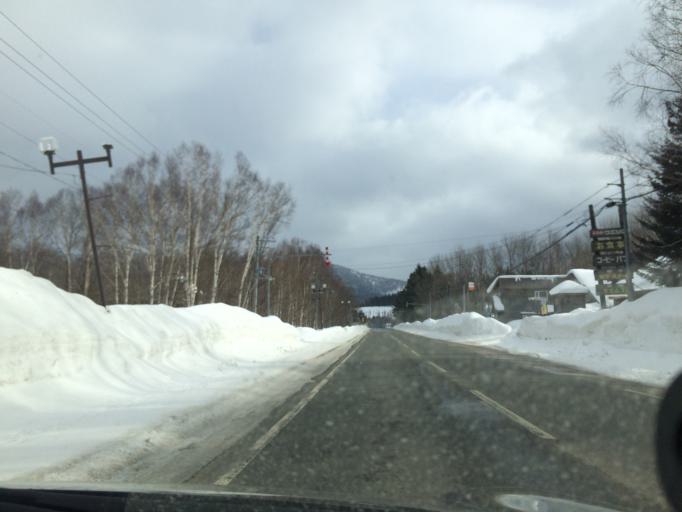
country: JP
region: Hokkaido
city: Shimo-furano
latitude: 43.0469
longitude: 142.6505
